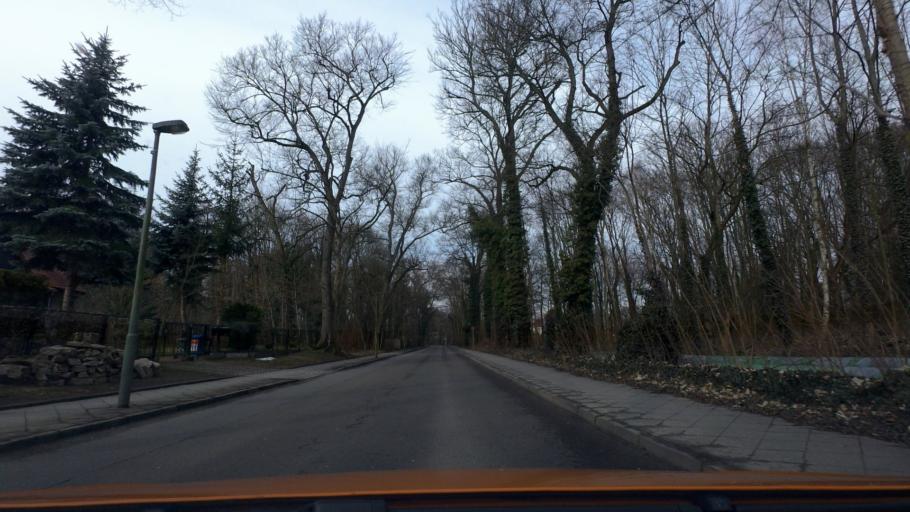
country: DE
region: Berlin
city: Buch
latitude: 52.6384
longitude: 13.5012
